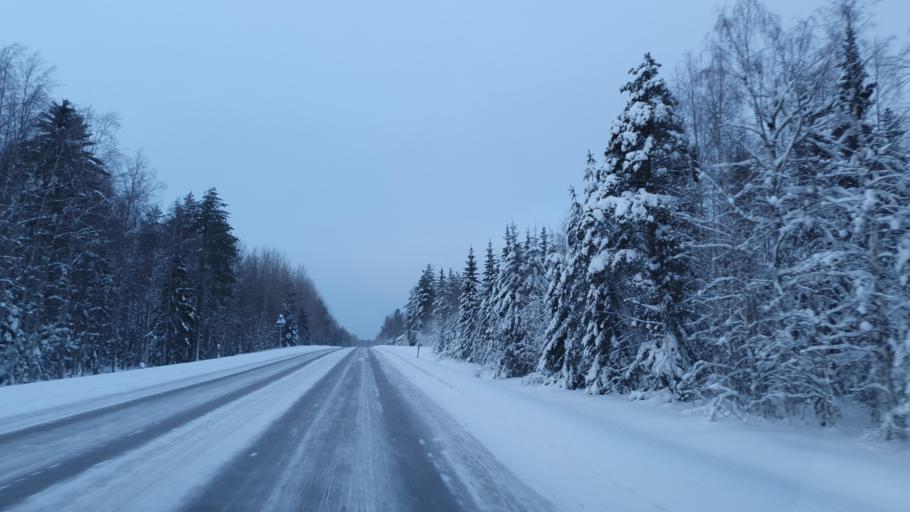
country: FI
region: Kainuu
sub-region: Kajaani
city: Kajaani
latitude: 64.4665
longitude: 27.4768
